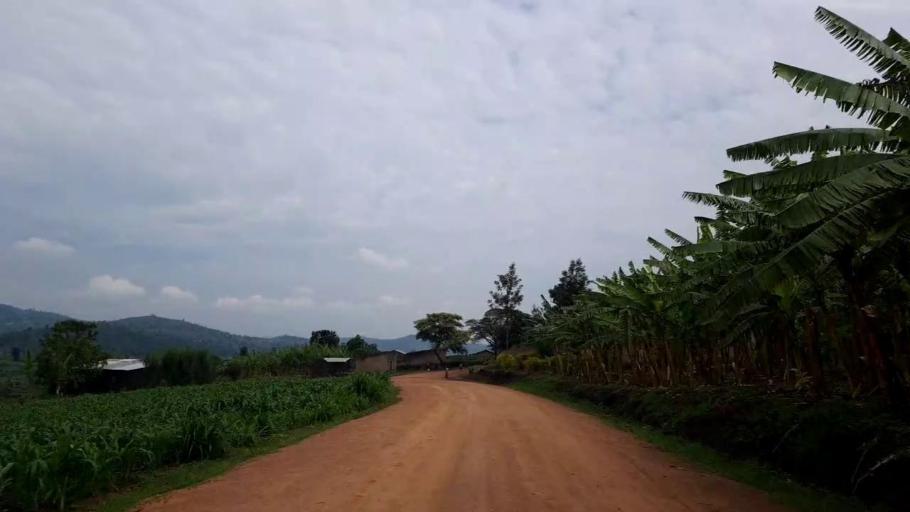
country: RW
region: Northern Province
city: Byumba
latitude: -1.4994
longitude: 30.2325
